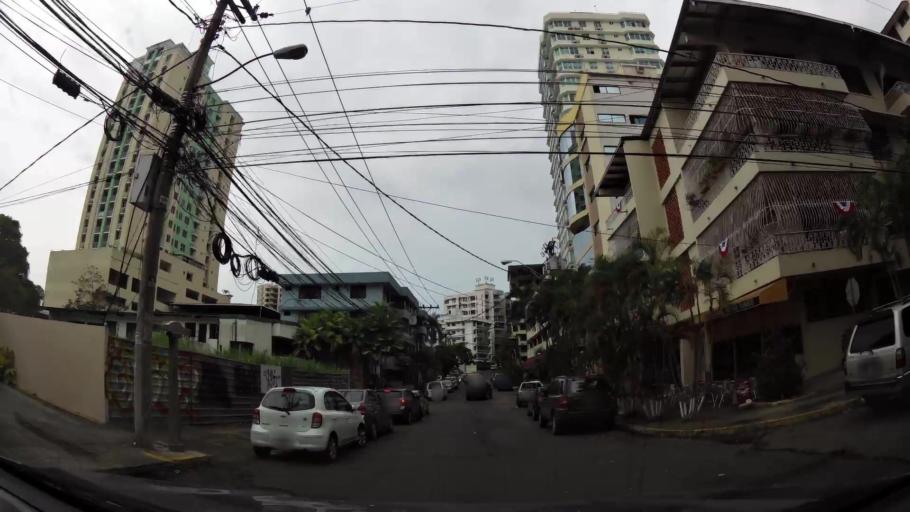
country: PA
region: Panama
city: Panama
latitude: 8.9869
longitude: -79.5299
